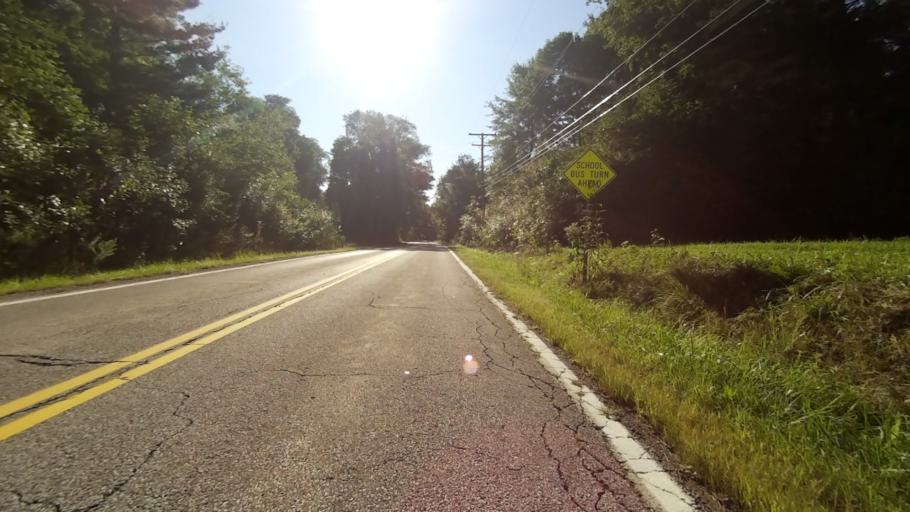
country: US
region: Ohio
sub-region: Portage County
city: Aurora
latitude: 41.3005
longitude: -81.2993
